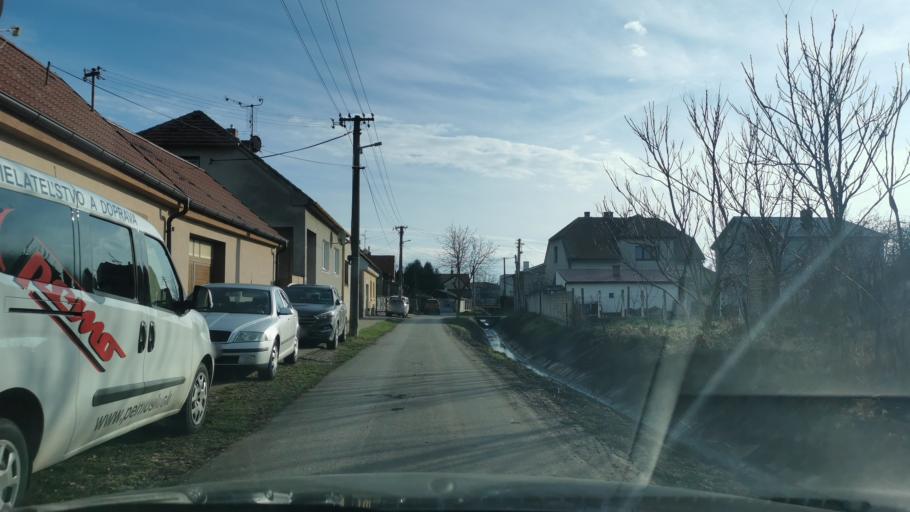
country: SK
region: Trnavsky
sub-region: Okres Skalica
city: Holic
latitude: 48.7915
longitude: 17.1225
